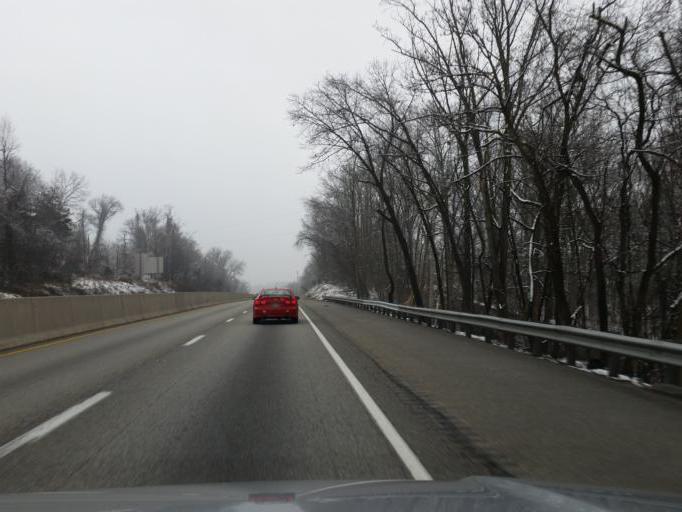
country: US
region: Pennsylvania
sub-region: York County
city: Valley Green
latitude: 40.1149
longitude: -76.7862
